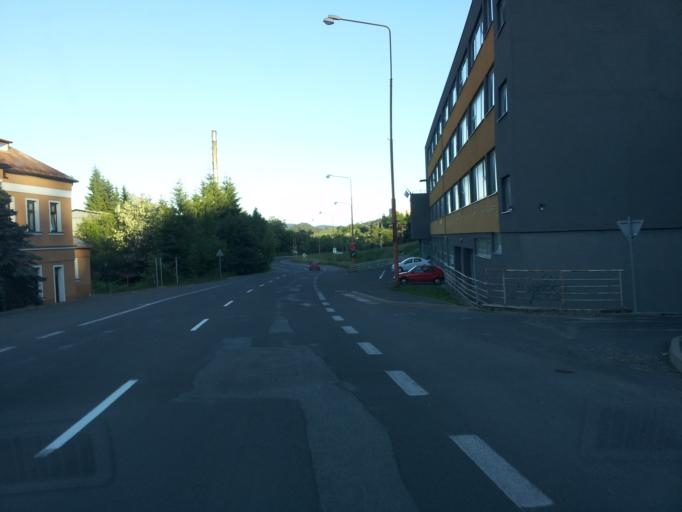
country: SK
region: Banskobystricky
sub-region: Okres Banska Bystrica
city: Banska Stiavnica
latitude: 48.4457
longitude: 18.9099
